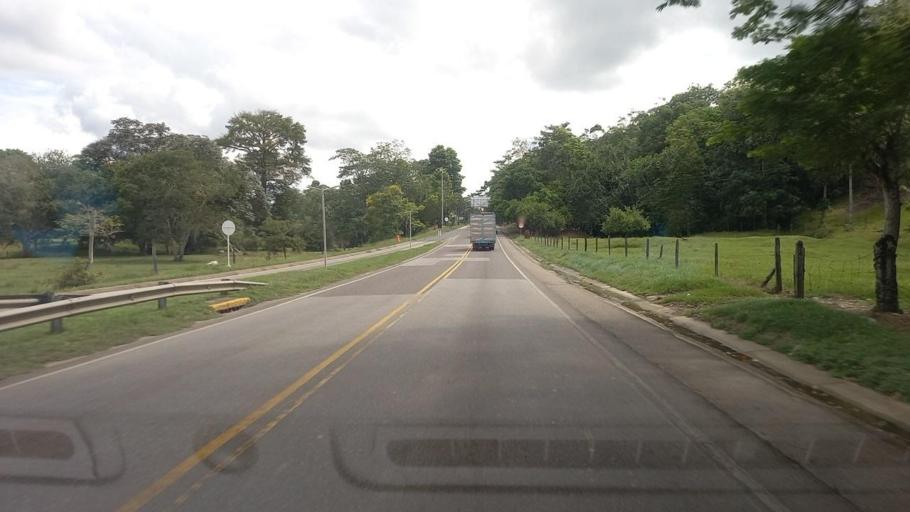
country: CO
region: Santander
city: Sabana de Torres
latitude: 7.1256
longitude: -73.5800
